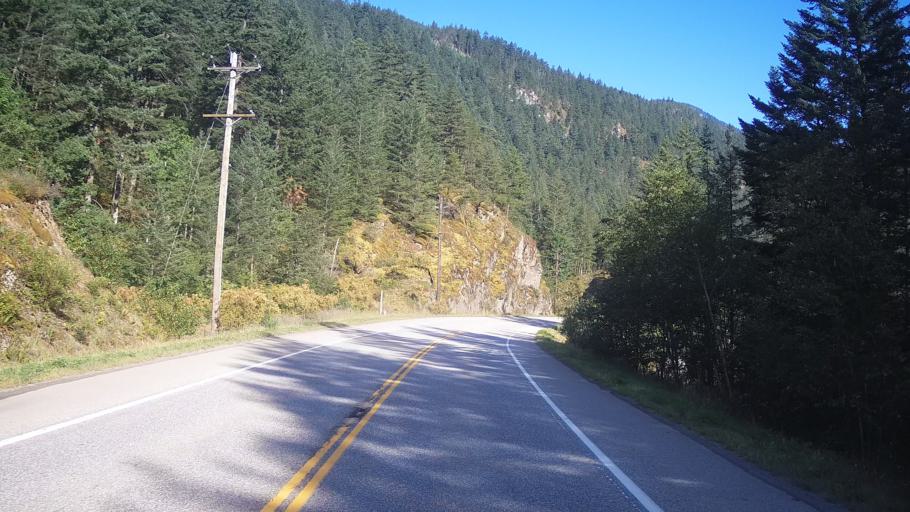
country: CA
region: British Columbia
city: Hope
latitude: 49.5961
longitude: -121.4125
